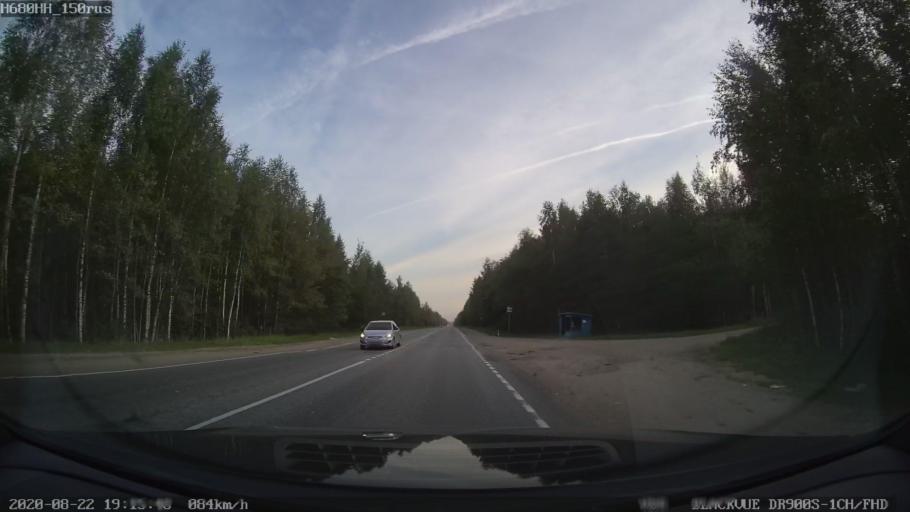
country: RU
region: Tverskaya
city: Sakharovo
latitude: 56.9633
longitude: 36.0207
